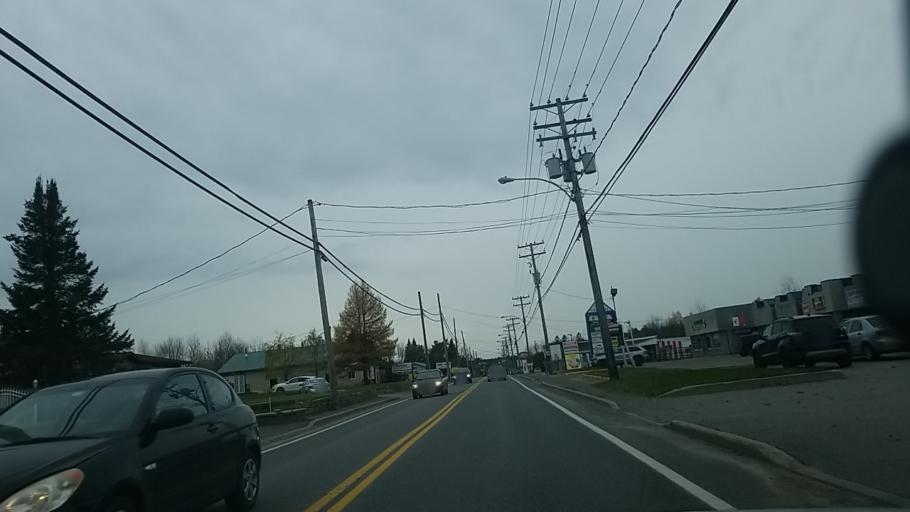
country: CA
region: Quebec
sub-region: Laurentides
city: Saint-Jerome
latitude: 45.7861
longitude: -74.0759
